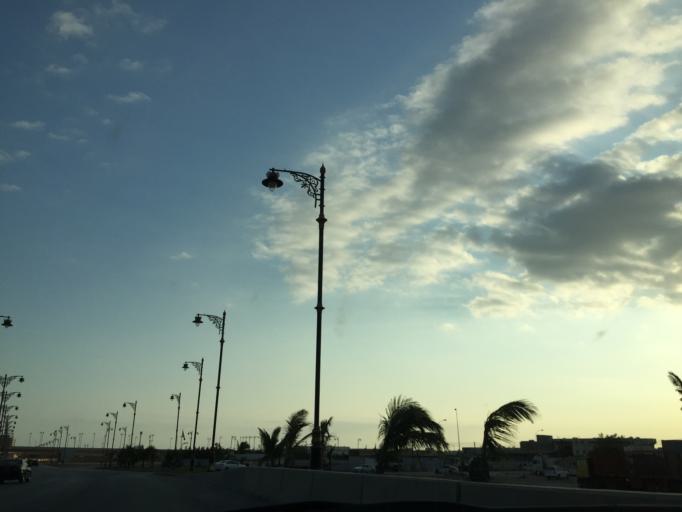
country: OM
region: Zufar
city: Salalah
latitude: 17.0218
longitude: 54.0573
